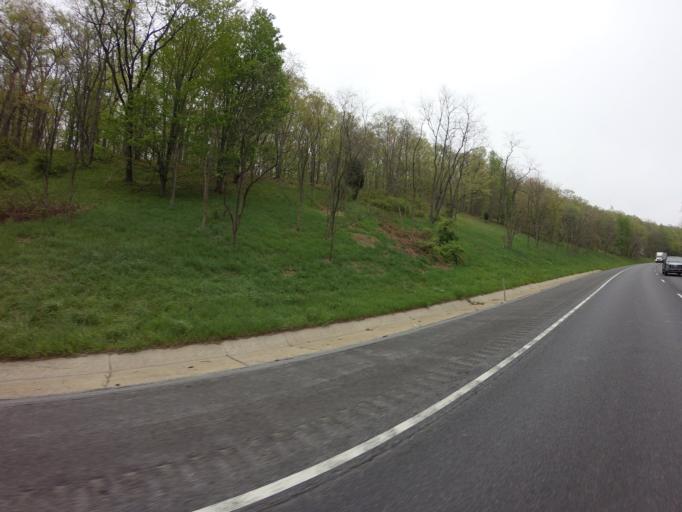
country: US
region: Maryland
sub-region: Washington County
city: Boonsboro
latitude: 39.5544
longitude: -77.6100
